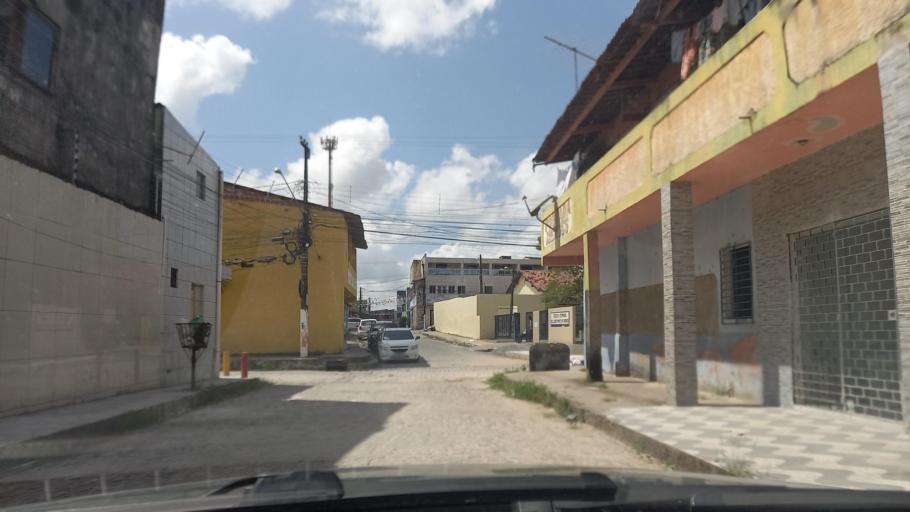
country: BR
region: Pernambuco
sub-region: Goiana
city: Goiana
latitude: -7.5615
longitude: -34.9930
